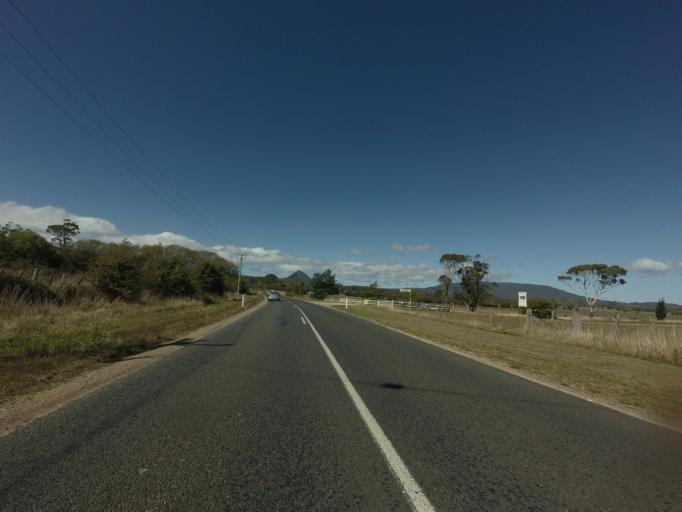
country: AU
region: Tasmania
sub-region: Break O'Day
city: St Helens
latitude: -41.5789
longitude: 148.1627
